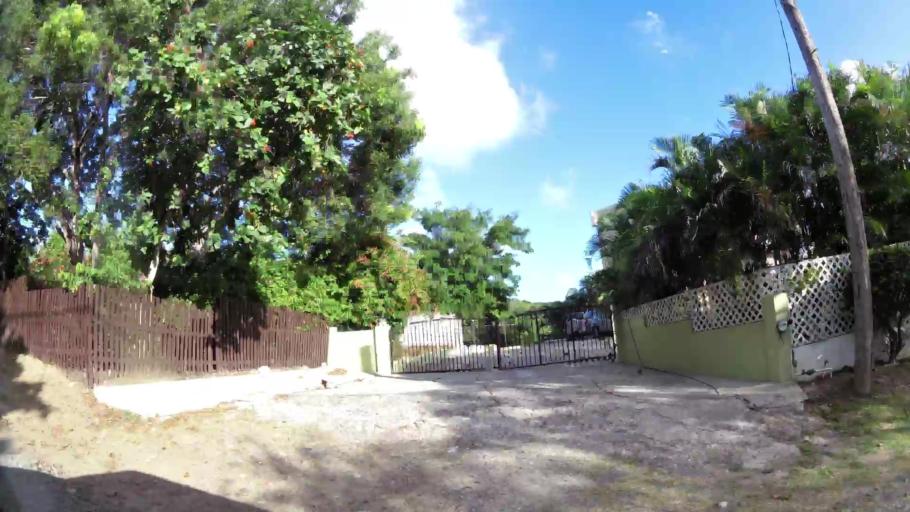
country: LC
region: Gros-Islet
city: Gros Islet
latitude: 14.1013
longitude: -60.9368
